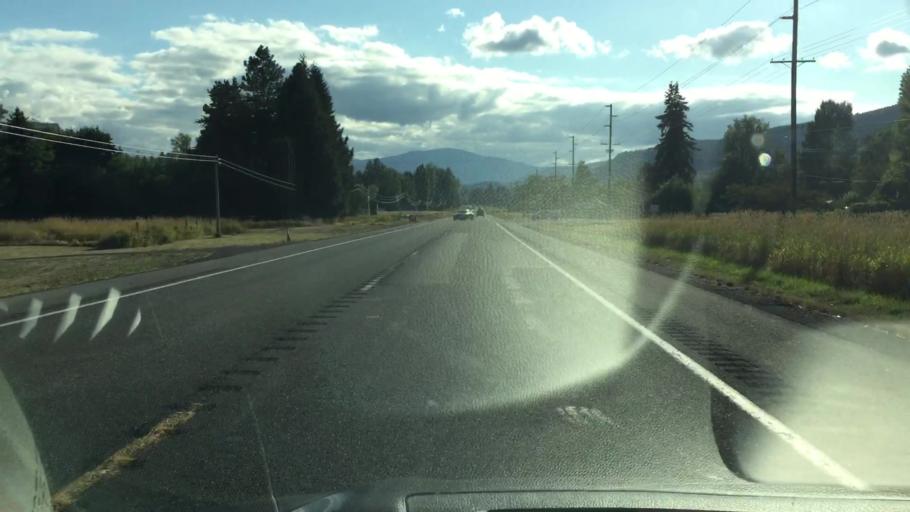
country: US
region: Washington
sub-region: Lewis County
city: Morton
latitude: 46.5311
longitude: -122.1307
